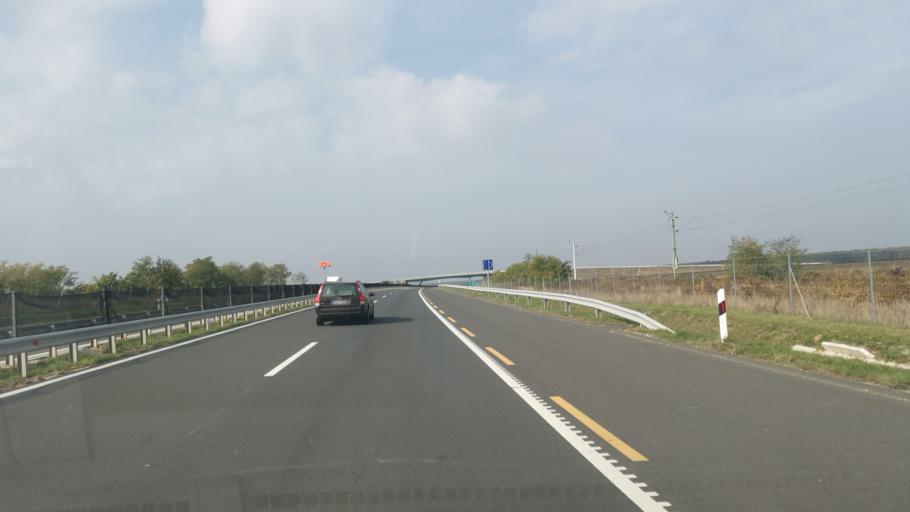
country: HU
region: Gyor-Moson-Sopron
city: Nagycenk
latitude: 47.6066
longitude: 16.6722
